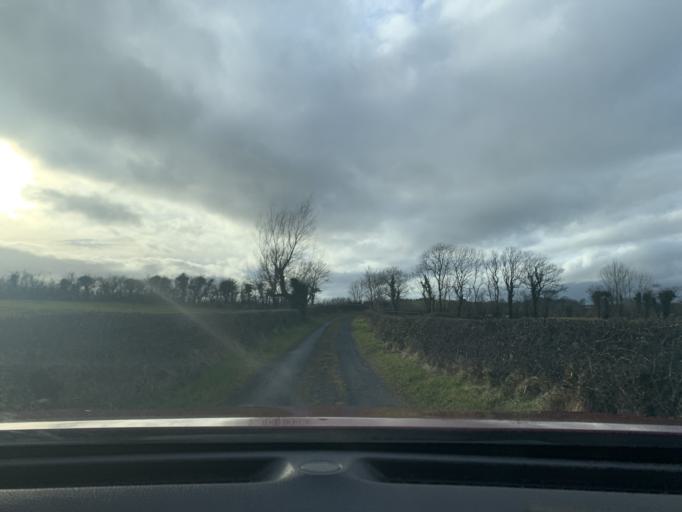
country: IE
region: Connaught
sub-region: Sligo
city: Ballymote
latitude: 54.0239
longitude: -8.5147
